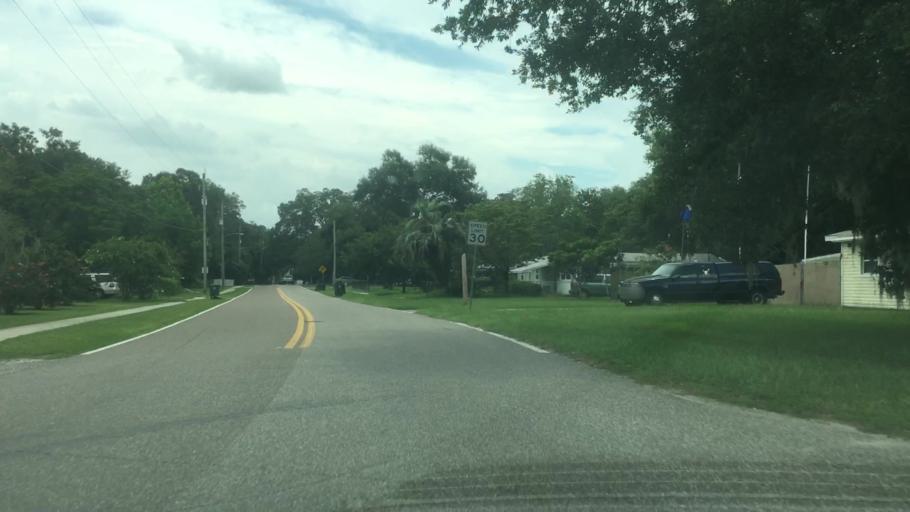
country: US
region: Florida
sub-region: Duval County
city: Jacksonville
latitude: 30.2948
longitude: -81.5500
